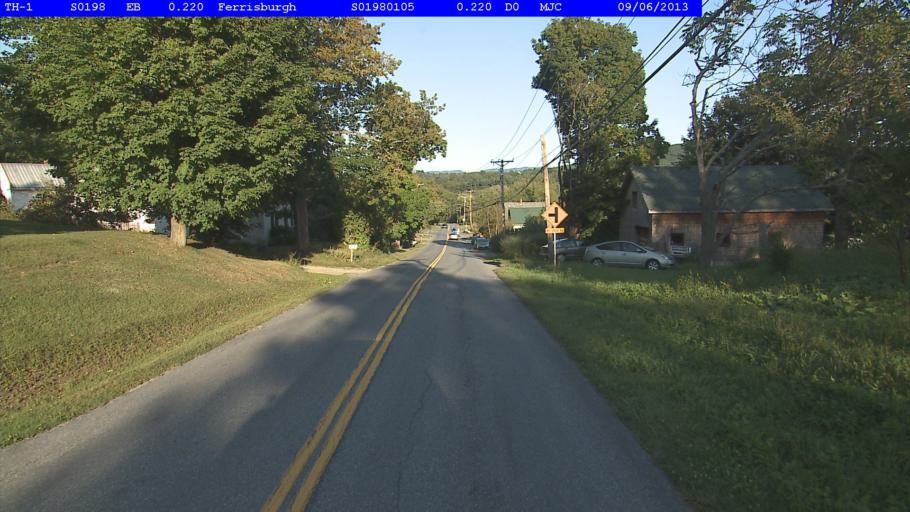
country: US
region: Vermont
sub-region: Addison County
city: Vergennes
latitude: 44.2586
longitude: -73.2238
